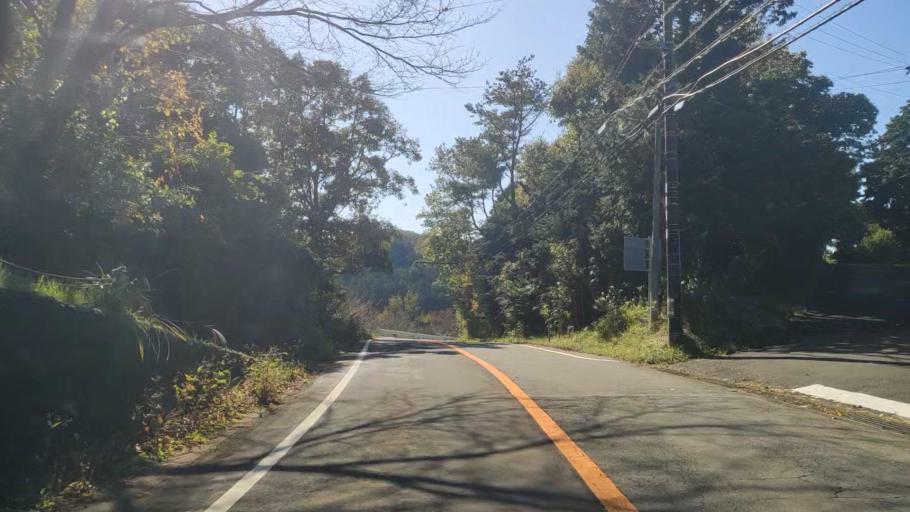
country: JP
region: Shizuoka
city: Atami
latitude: 35.0244
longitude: 139.0123
